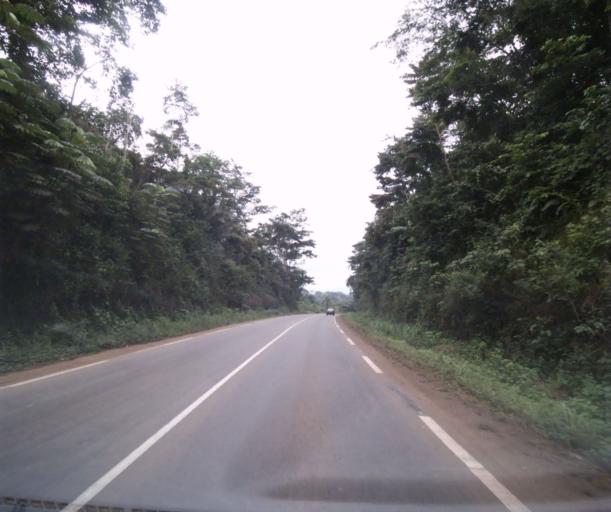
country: CM
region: Centre
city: Mbankomo
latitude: 3.7821
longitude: 11.2788
